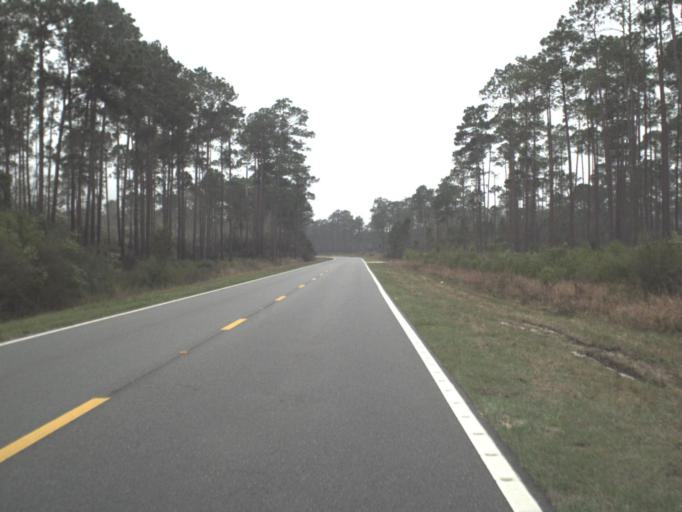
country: US
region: Florida
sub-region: Liberty County
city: Bristol
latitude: 30.3141
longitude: -84.8283
